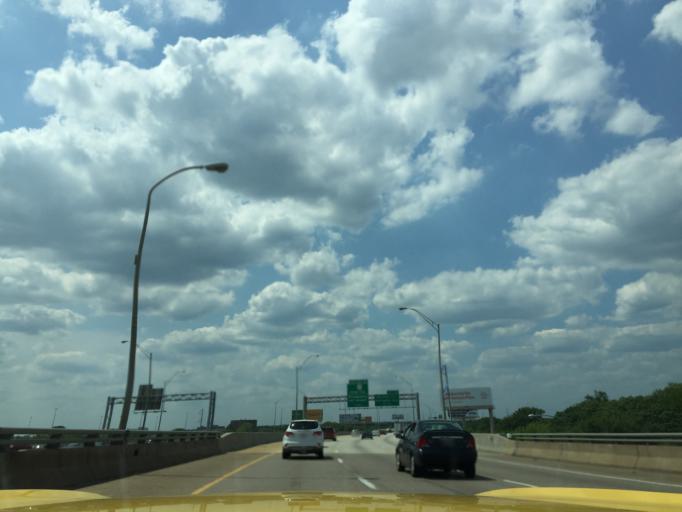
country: US
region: New Jersey
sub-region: Gloucester County
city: National Park
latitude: 39.8864
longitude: -75.2134
